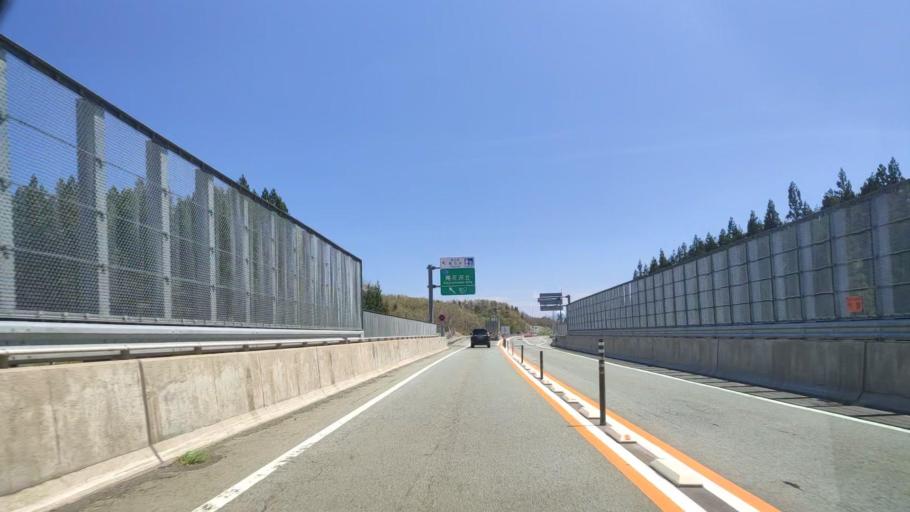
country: JP
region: Yamagata
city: Obanazawa
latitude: 38.6618
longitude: 140.3603
